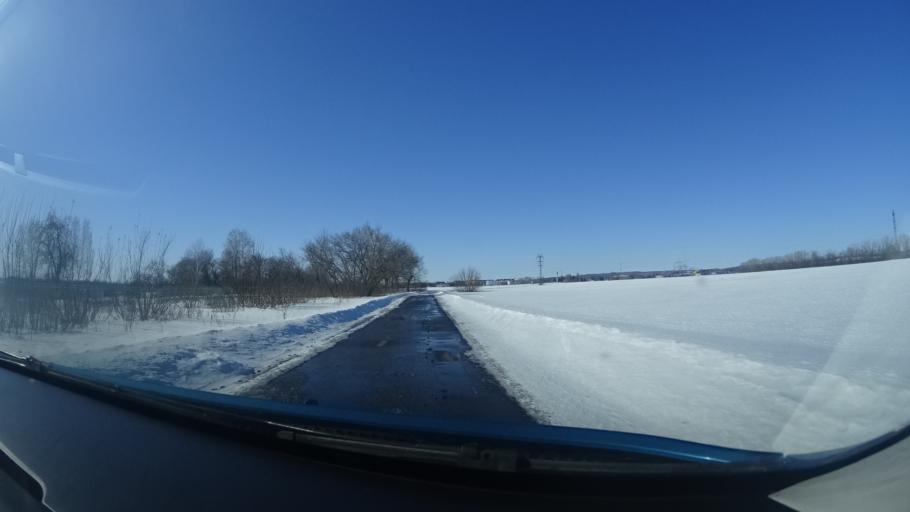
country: RU
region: Bashkortostan
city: Chishmy
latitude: 54.5827
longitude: 55.4171
